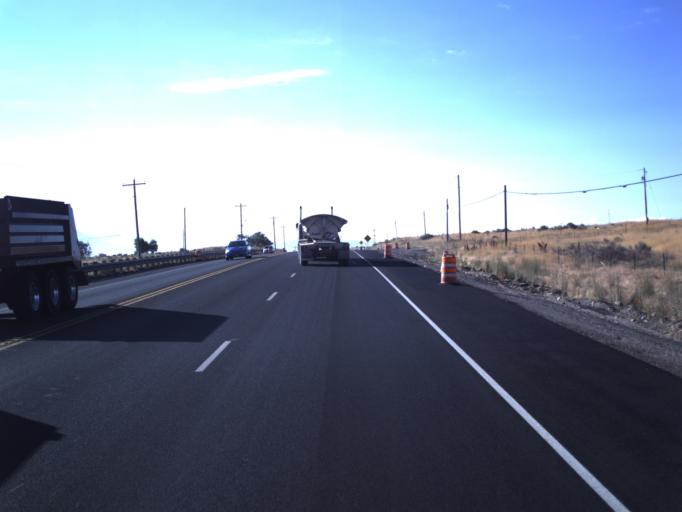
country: US
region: Utah
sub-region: Salt Lake County
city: Oquirrh
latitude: 40.6473
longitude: -112.0687
